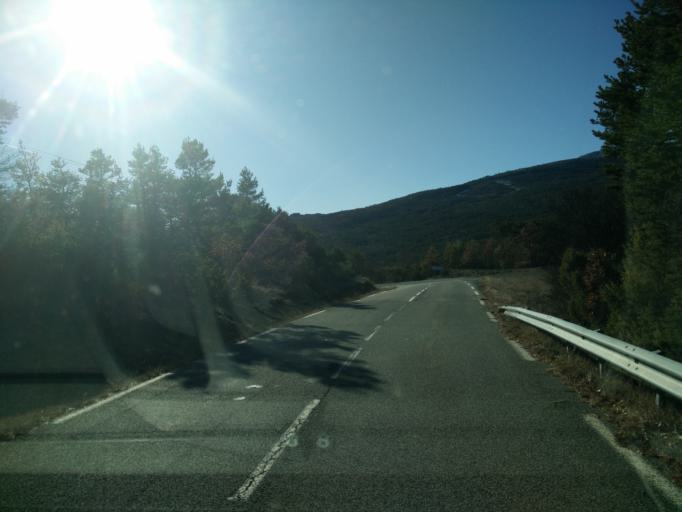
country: FR
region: Provence-Alpes-Cote d'Azur
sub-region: Departement des Alpes-de-Haute-Provence
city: Castellane
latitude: 43.7813
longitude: 6.4449
